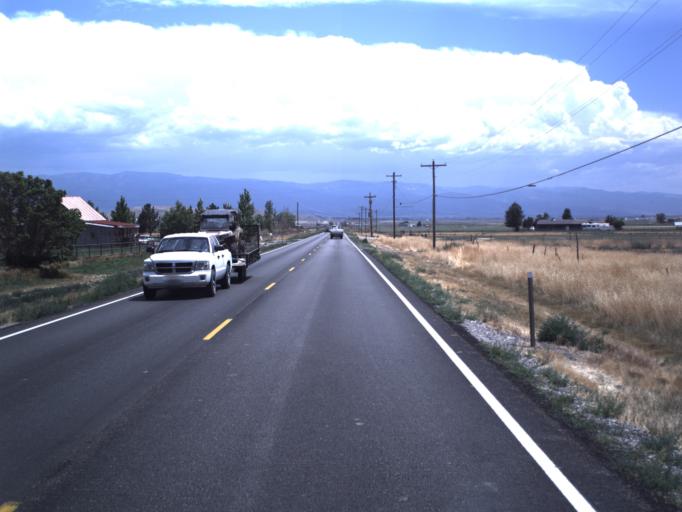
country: US
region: Utah
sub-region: Sanpete County
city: Fountain Green
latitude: 39.6064
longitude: -111.6247
